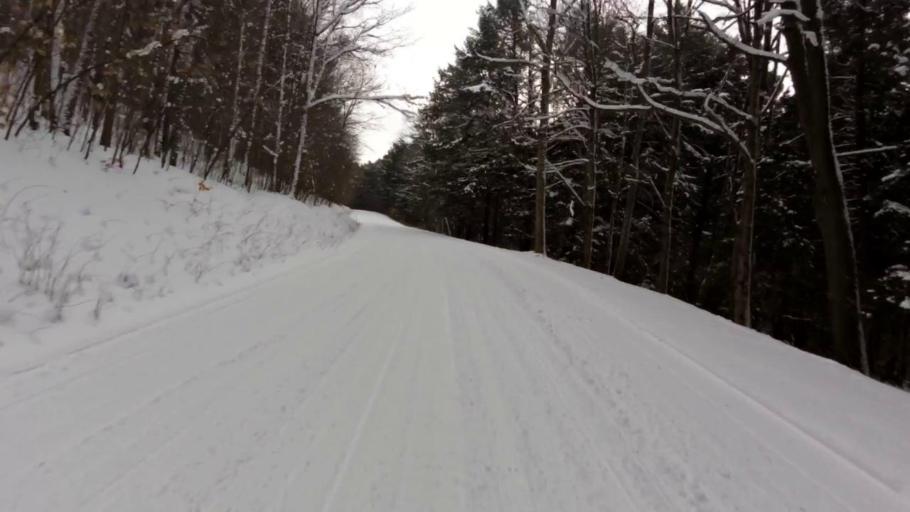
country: US
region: New York
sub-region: Cattaraugus County
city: Salamanca
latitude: 42.0611
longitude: -78.7639
